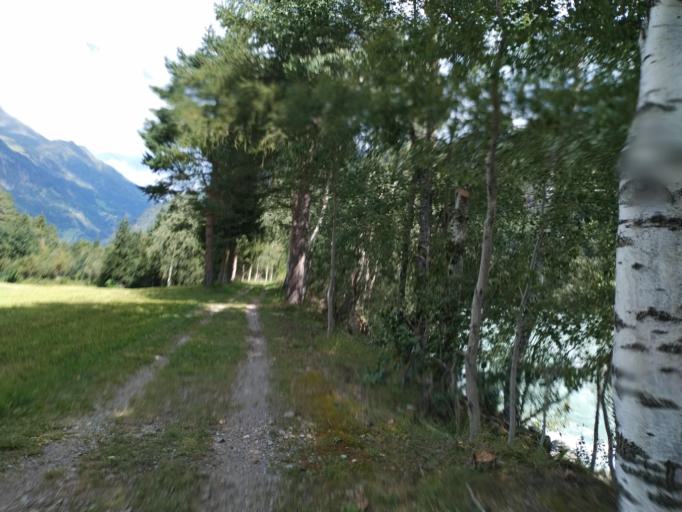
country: AT
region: Tyrol
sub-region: Politischer Bezirk Lienz
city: Schlaiten
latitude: 46.9167
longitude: 12.6061
